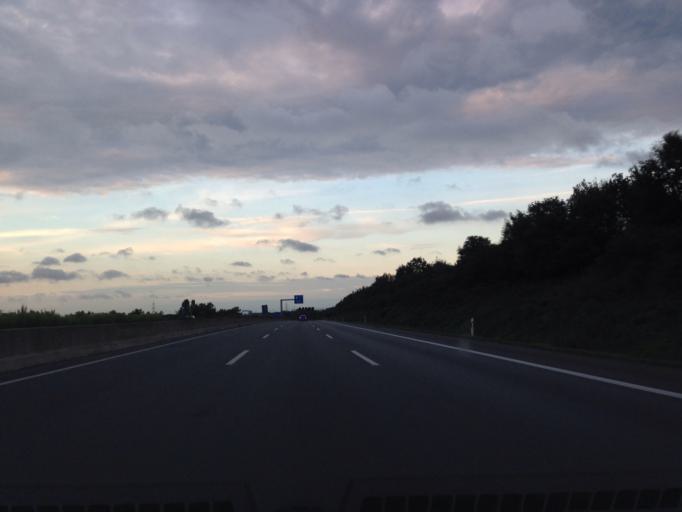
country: DE
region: North Rhine-Westphalia
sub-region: Regierungsbezirk Dusseldorf
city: Kaarst
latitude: 51.2518
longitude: 6.6403
